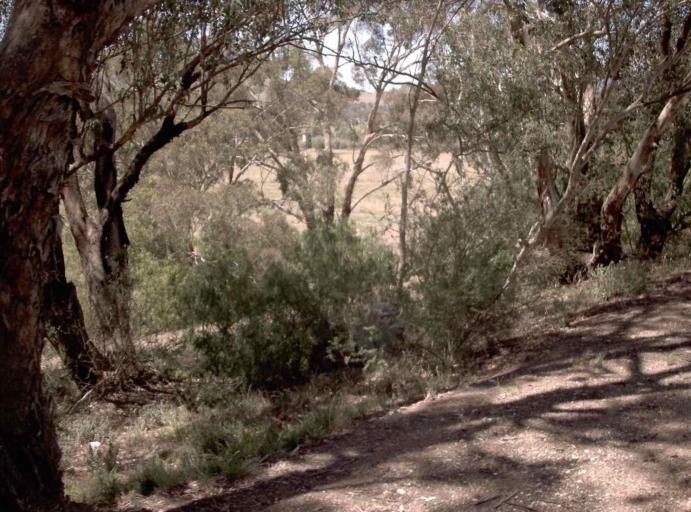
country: AU
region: Victoria
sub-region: East Gippsland
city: Bairnsdale
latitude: -37.2121
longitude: 147.7175
